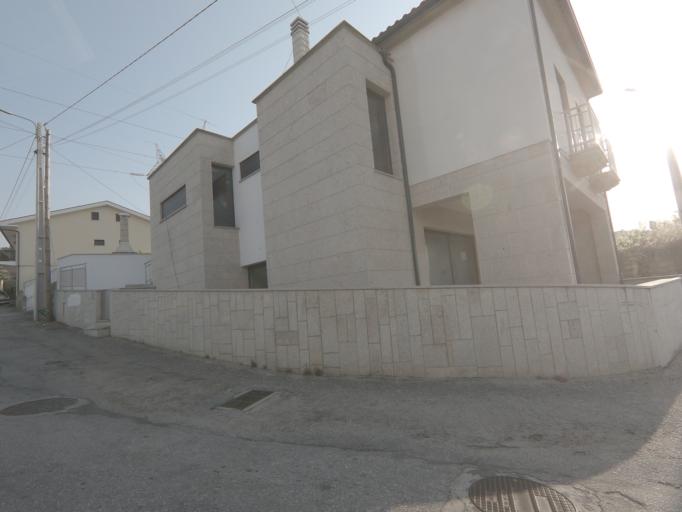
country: PT
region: Viseu
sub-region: Tabuaco
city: Tabuaco
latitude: 41.1443
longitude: -7.6071
